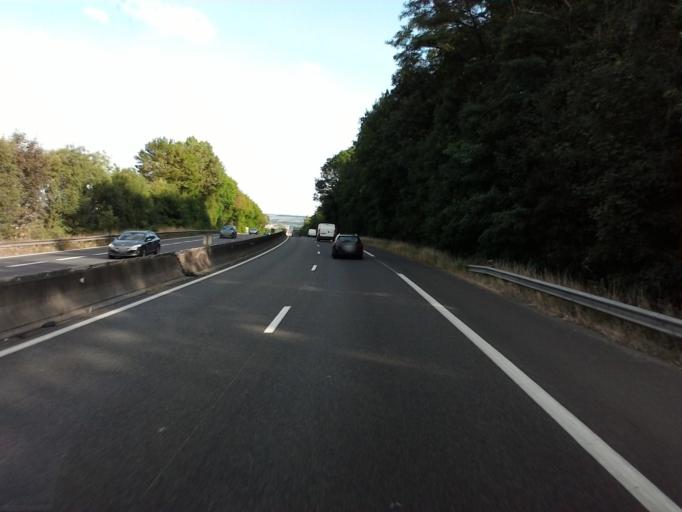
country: FR
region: Lorraine
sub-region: Departement de Meurthe-et-Moselle
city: Ludres
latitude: 48.6363
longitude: 6.1716
